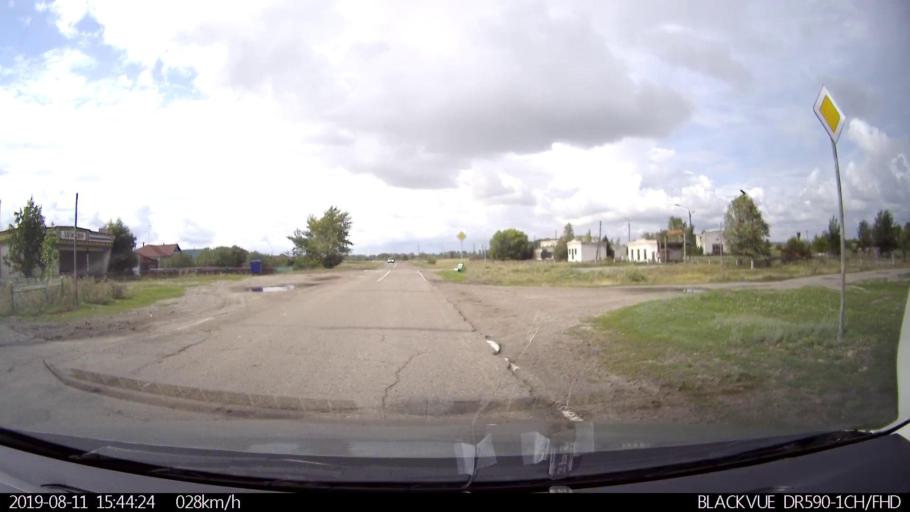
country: RU
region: Ulyanovsk
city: Ignatovka
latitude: 53.8816
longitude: 47.6568
